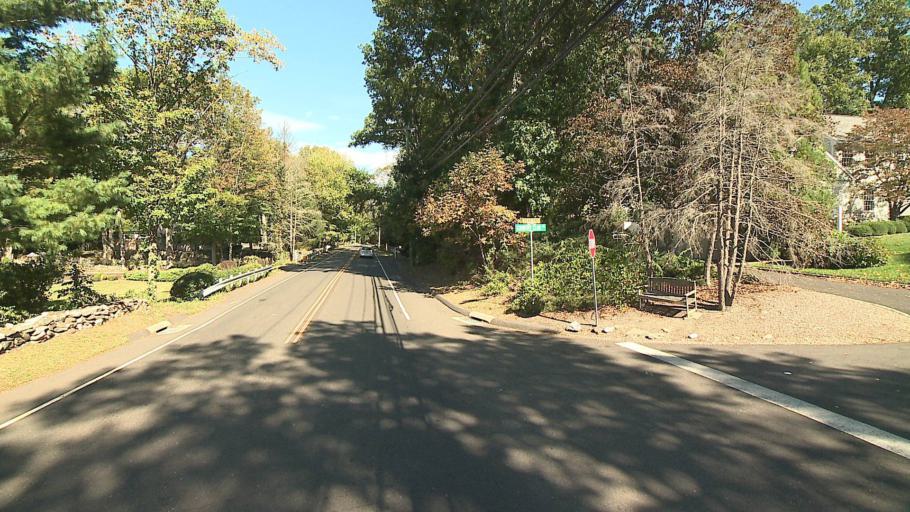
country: US
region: Connecticut
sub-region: Fairfield County
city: New Canaan
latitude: 41.1101
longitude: -73.5010
